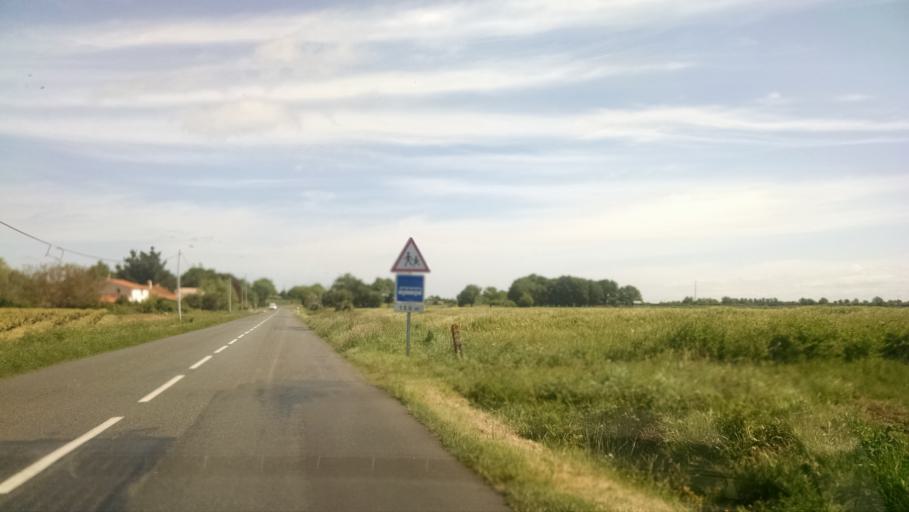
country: FR
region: Pays de la Loire
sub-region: Departement de la Loire-Atlantique
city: Saint-Hilaire-de-Clisson
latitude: 47.0514
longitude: -1.3198
